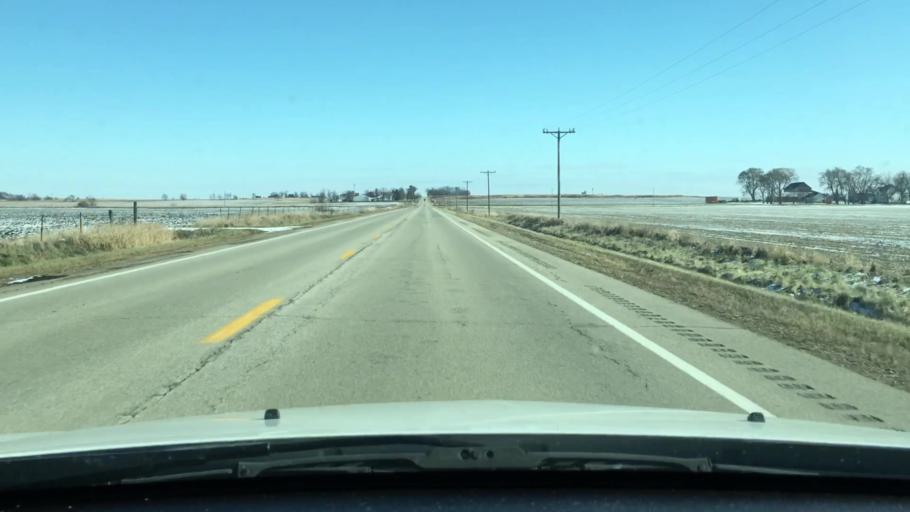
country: US
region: Illinois
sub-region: DeKalb County
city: Malta
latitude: 42.0008
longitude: -88.9226
